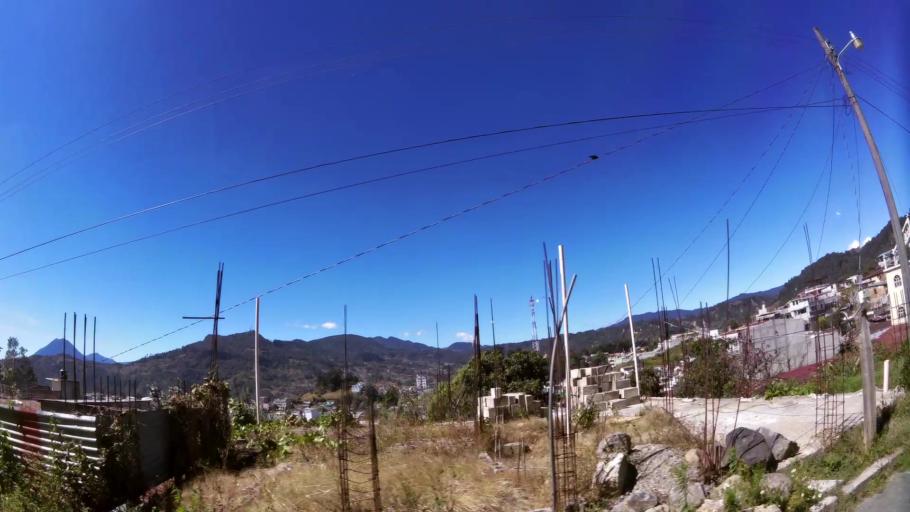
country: GT
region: Solola
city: Solola
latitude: 14.7749
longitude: -91.1807
